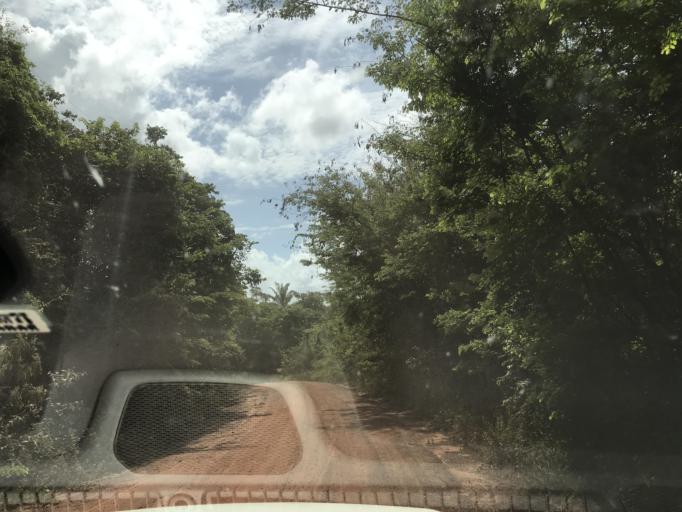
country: BR
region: Bahia
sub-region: Entre Rios
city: Entre Rios
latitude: -12.1644
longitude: -38.0743
